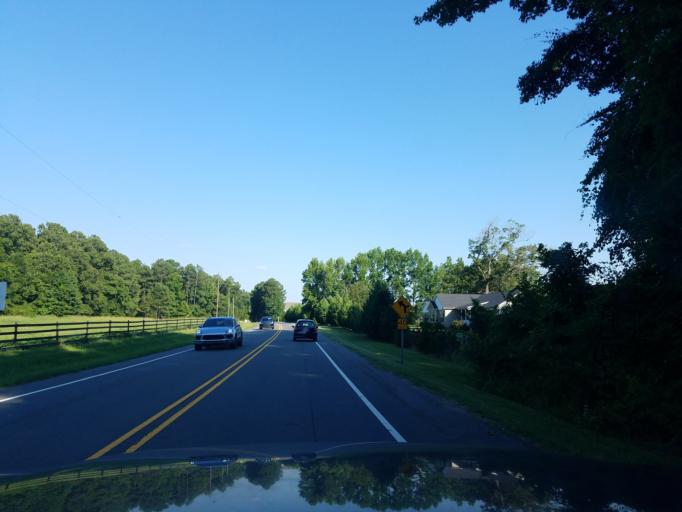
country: US
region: North Carolina
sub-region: Orange County
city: Chapel Hill
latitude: 35.8854
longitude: -78.9747
